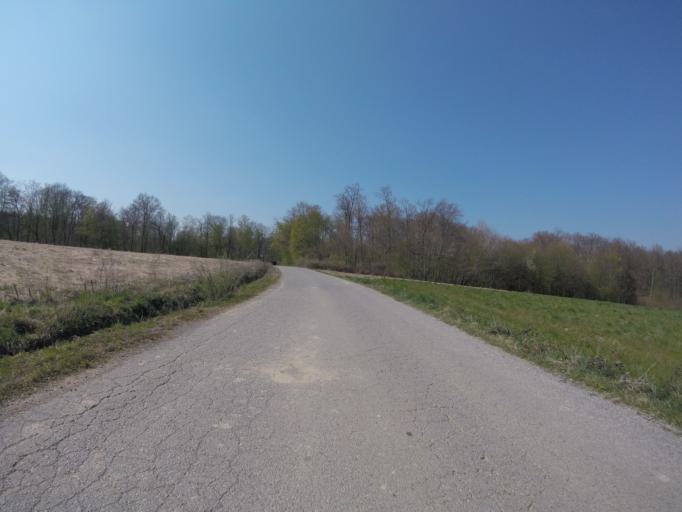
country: HR
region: Grad Zagreb
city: Strmec
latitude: 45.5621
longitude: 15.9056
